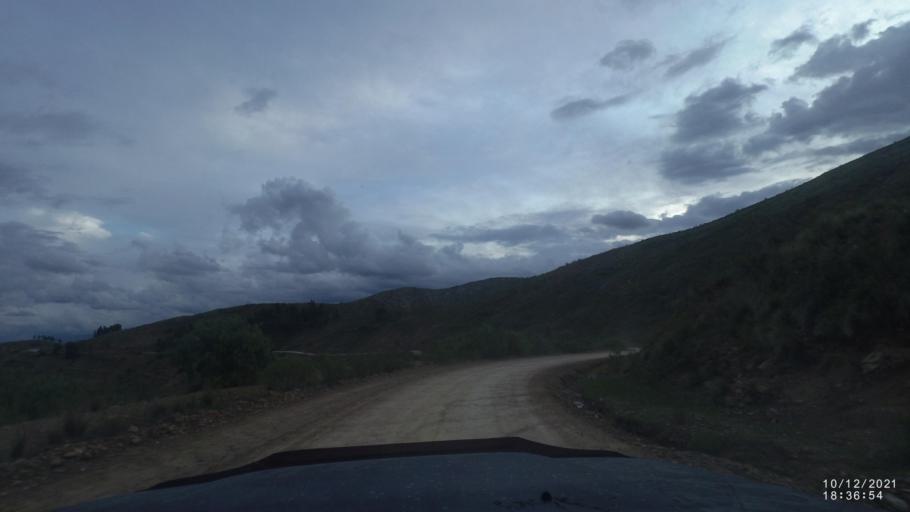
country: BO
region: Cochabamba
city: Tarata
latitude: -17.8350
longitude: -65.9919
